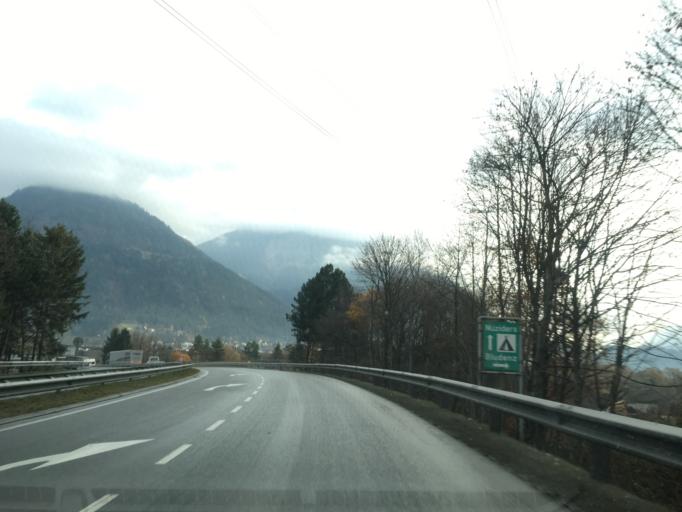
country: AT
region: Vorarlberg
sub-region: Politischer Bezirk Bludenz
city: Nuziders
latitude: 47.1651
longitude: 9.7900
